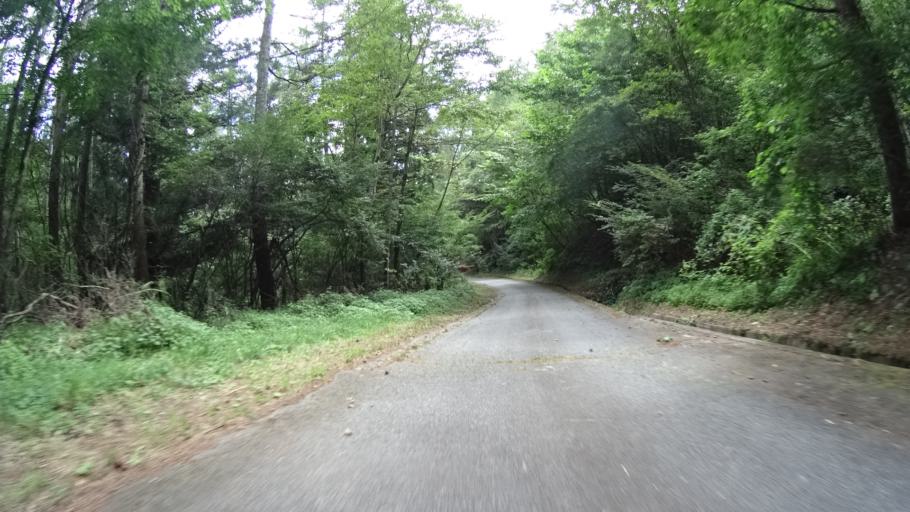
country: JP
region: Yamanashi
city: Nirasaki
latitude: 35.8010
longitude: 138.5269
